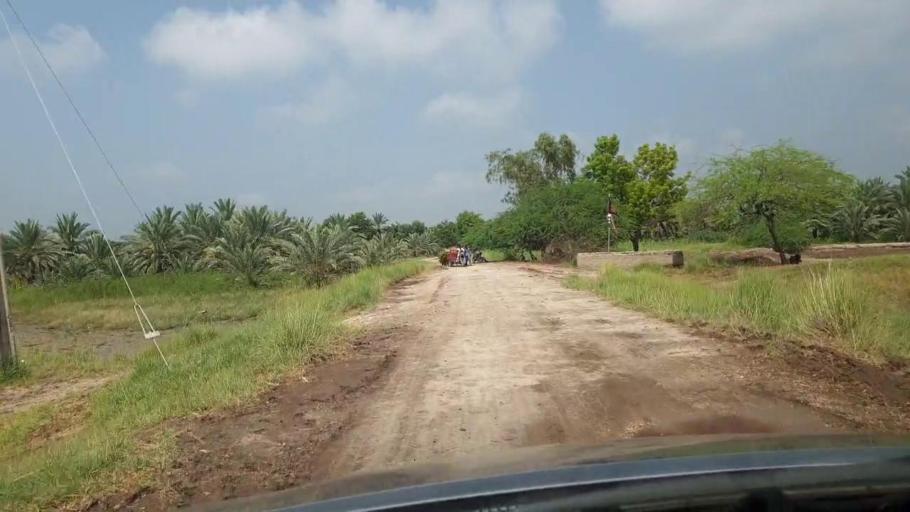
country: PK
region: Sindh
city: Pir jo Goth
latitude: 27.6055
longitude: 68.6949
